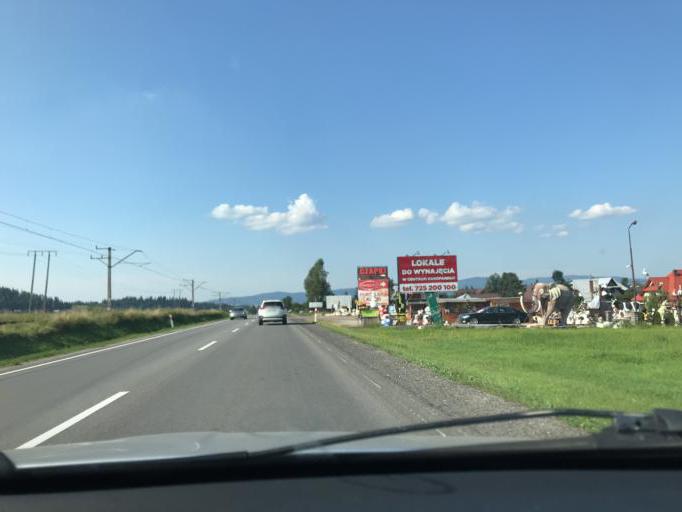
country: PL
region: Lesser Poland Voivodeship
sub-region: Powiat nowotarski
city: Szaflary
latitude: 49.4118
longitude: 20.0179
